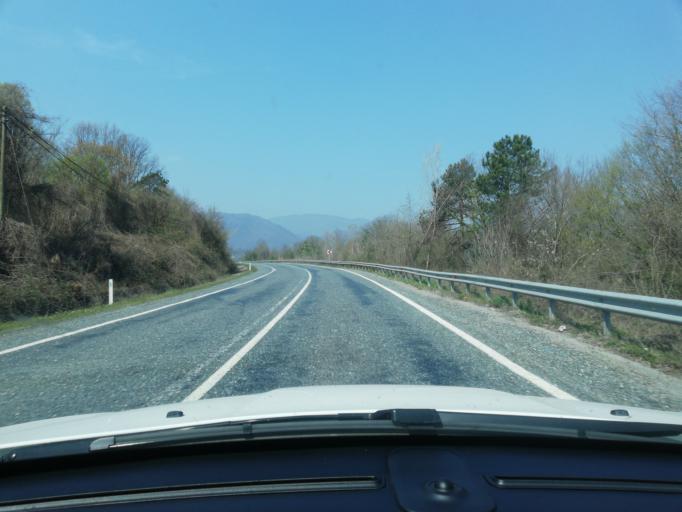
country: TR
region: Zonguldak
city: Gokcebey
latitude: 41.2288
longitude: 32.2080
